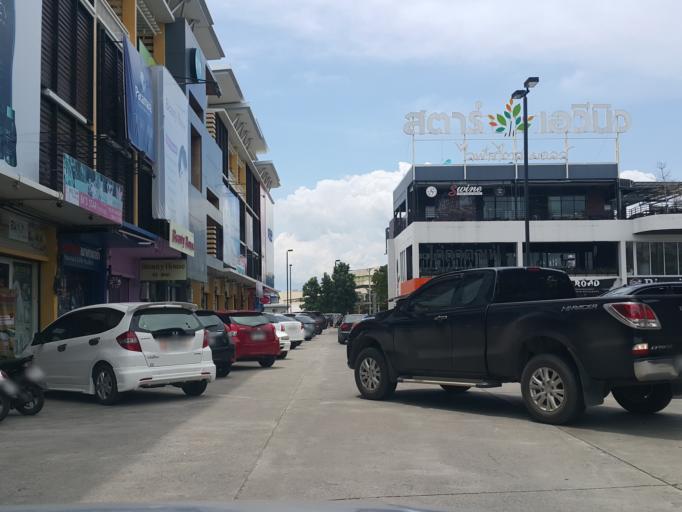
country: TH
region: Chiang Mai
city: Chiang Mai
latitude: 18.7999
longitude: 99.0195
